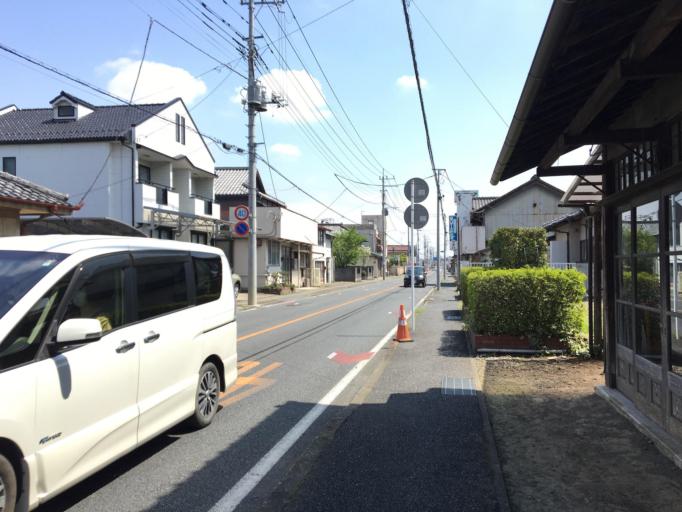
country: JP
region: Gunma
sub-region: Sawa-gun
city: Tamamura
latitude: 36.3030
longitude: 139.1124
